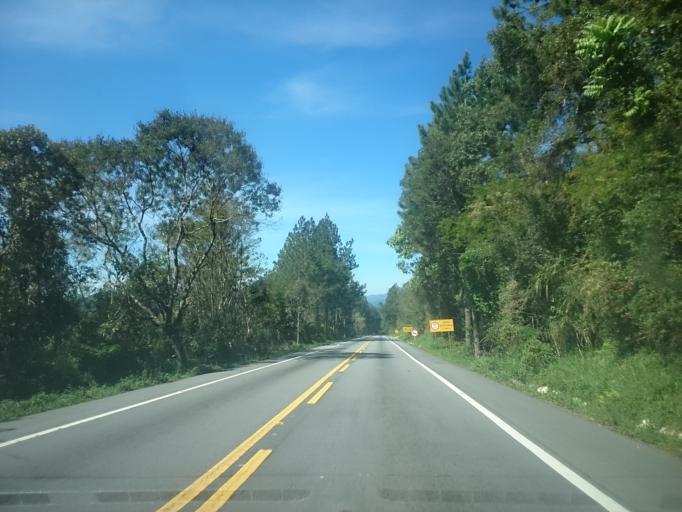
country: BR
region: Santa Catarina
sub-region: Santo Amaro Da Imperatriz
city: Santo Amaro da Imperatriz
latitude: -27.6949
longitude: -48.9684
